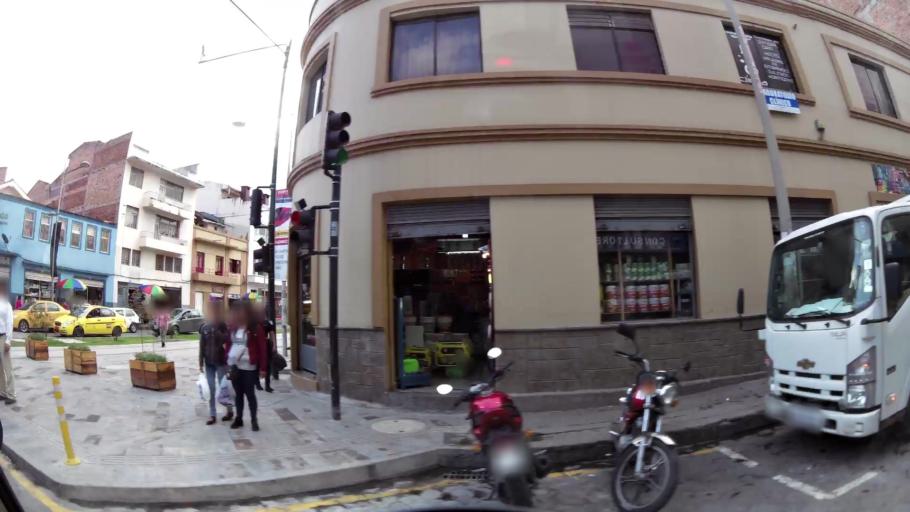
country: EC
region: Azuay
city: Cuenca
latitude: -2.8949
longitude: -78.9985
